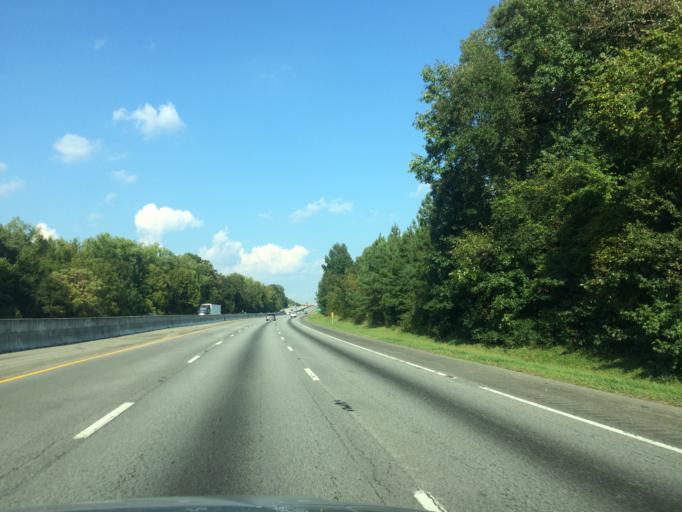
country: US
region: South Carolina
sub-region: Anderson County
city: Williamston
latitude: 34.6692
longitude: -82.5474
